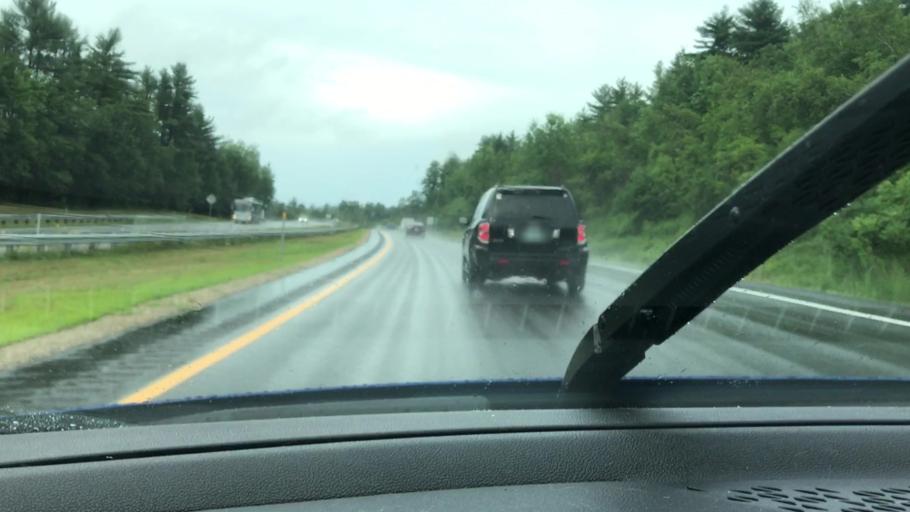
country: US
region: New Hampshire
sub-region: Merrimack County
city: Chichester
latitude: 43.2376
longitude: -71.4595
